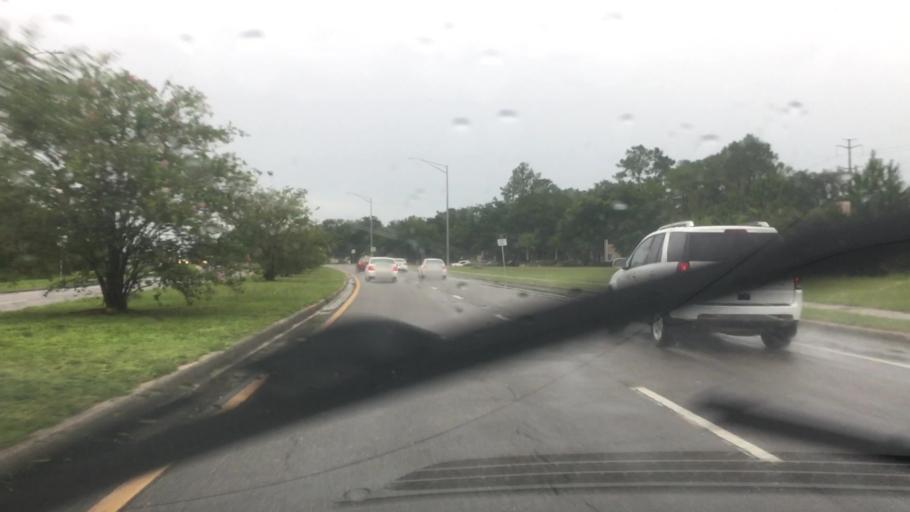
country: US
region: Florida
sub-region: Duval County
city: Jacksonville Beach
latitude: 30.2756
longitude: -81.5232
